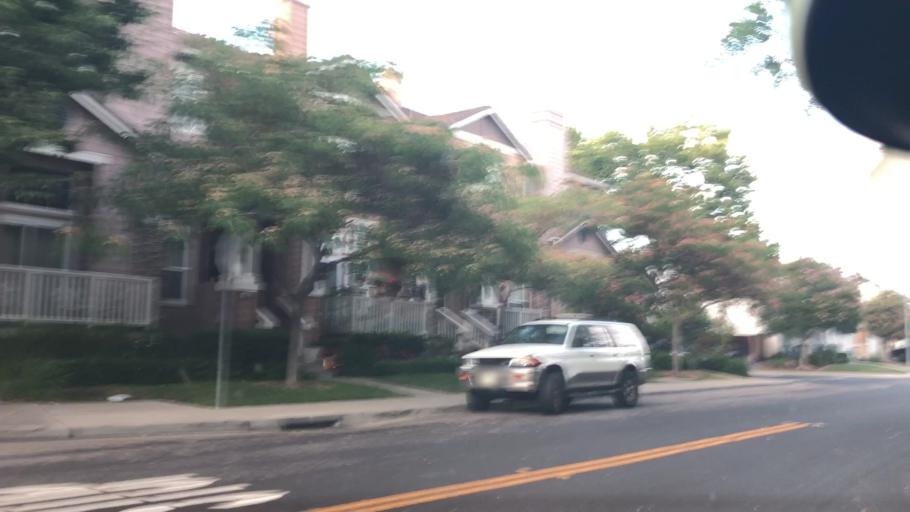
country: US
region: California
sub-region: Alameda County
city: Pleasanton
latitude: 37.7073
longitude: -121.8851
